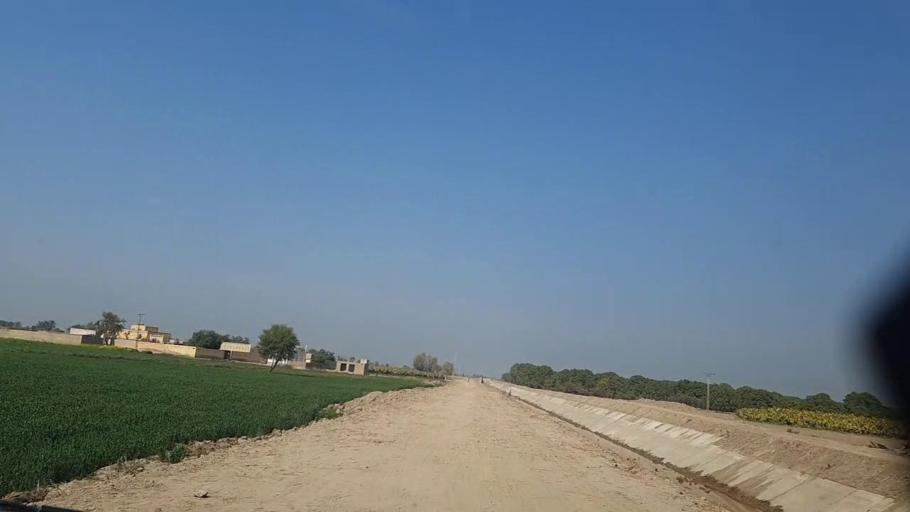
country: PK
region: Sindh
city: Sakrand
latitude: 26.1493
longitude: 68.3318
